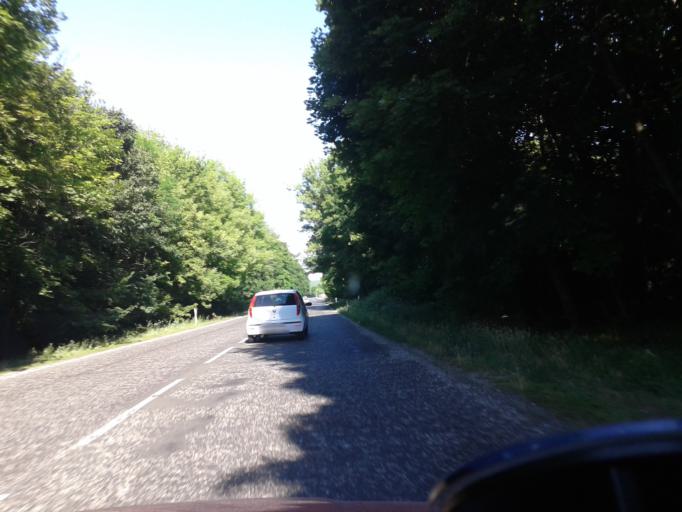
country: HU
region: Fejer
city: Etyek
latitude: 47.4954
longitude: 18.7296
